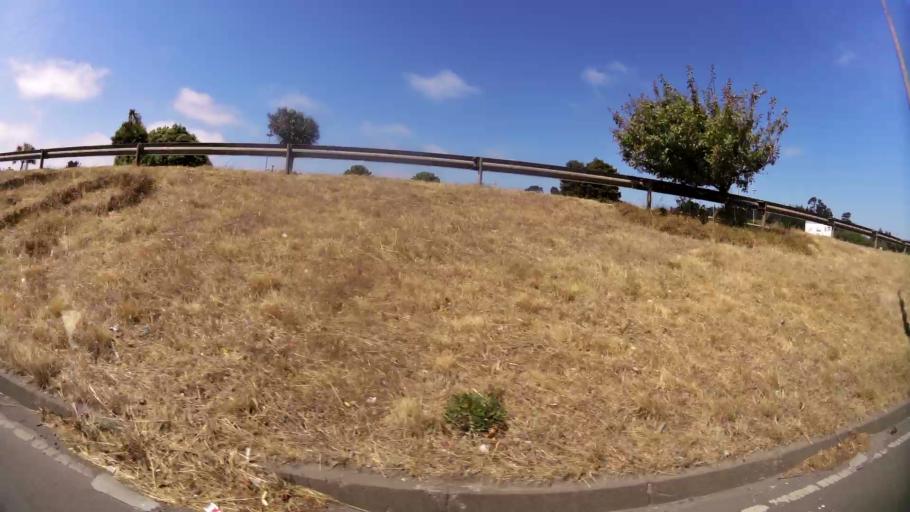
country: CL
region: Biobio
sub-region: Provincia de Concepcion
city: Concepcion
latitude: -36.7951
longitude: -73.0680
